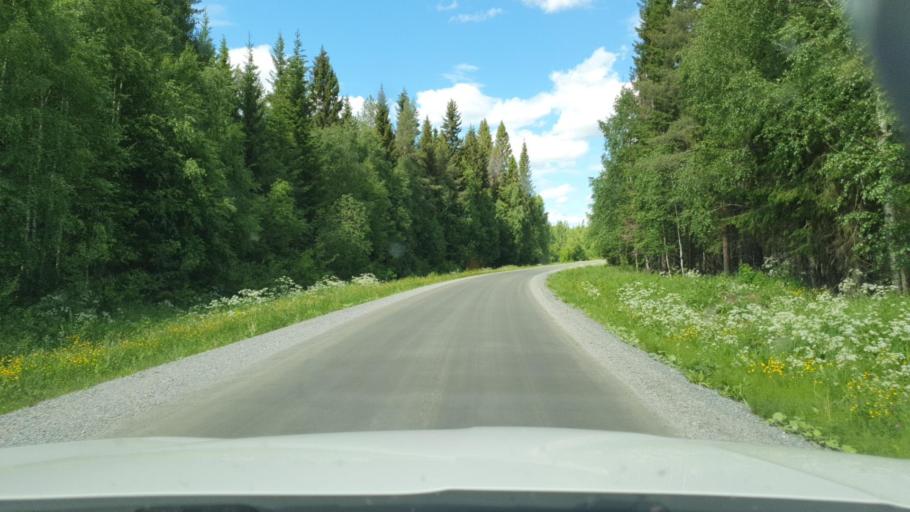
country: SE
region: Vaesterbotten
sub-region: Skelleftea Kommun
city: Forsbacka
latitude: 64.8145
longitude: 20.4935
